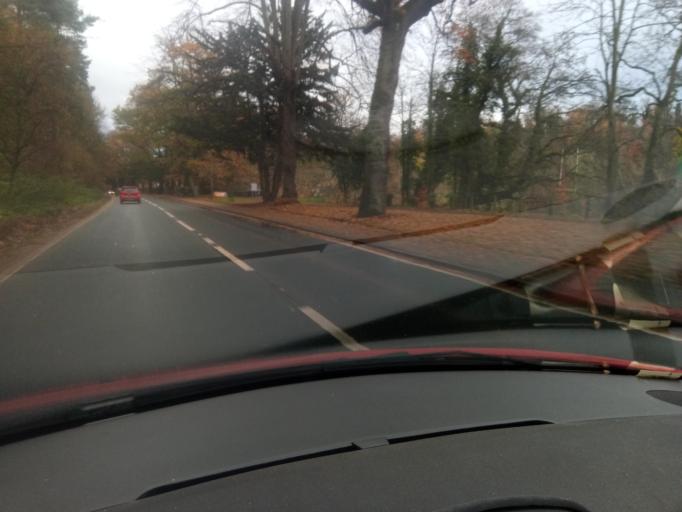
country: GB
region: Scotland
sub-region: The Scottish Borders
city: Jedburgh
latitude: 55.4903
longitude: -2.5450
